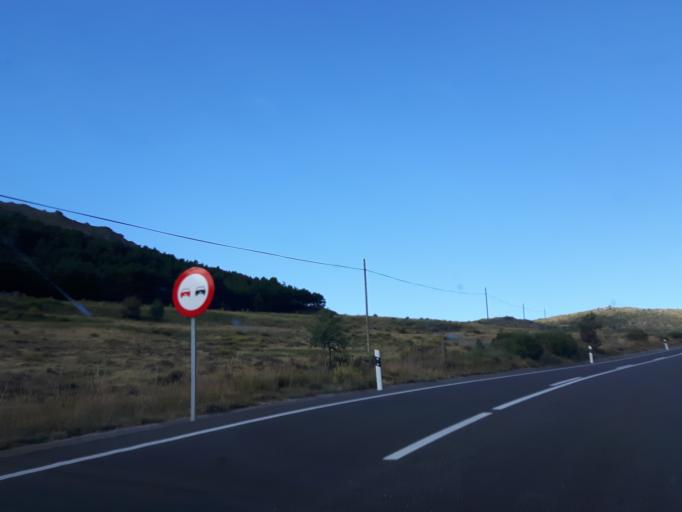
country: ES
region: Castille and Leon
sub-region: Provincia de Avila
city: Mengamunoz
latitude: 40.4959
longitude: -5.0033
